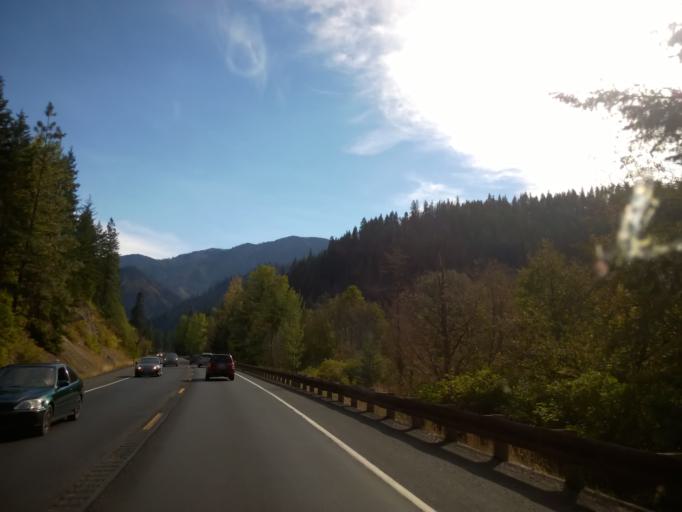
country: US
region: Washington
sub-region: Chelan County
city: Leavenworth
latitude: 47.7116
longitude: -120.7418
